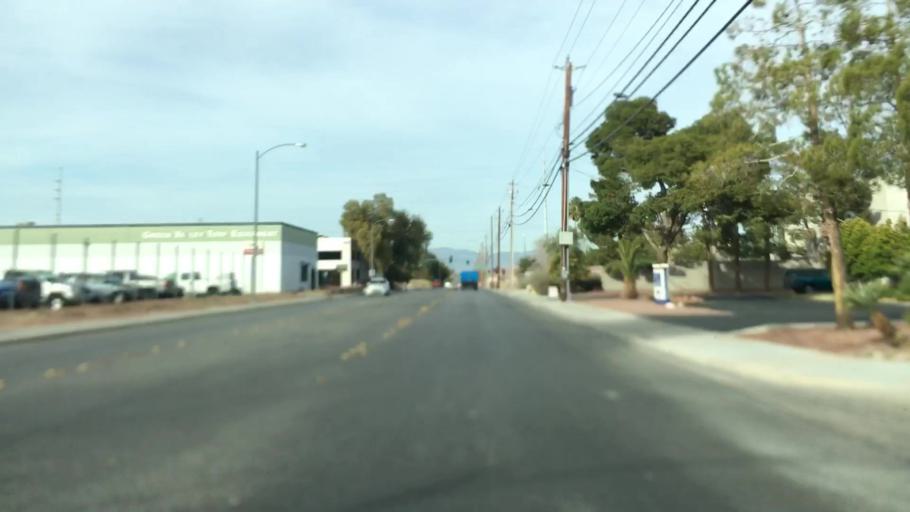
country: US
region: Nevada
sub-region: Clark County
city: Whitney
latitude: 36.0767
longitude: -115.0869
